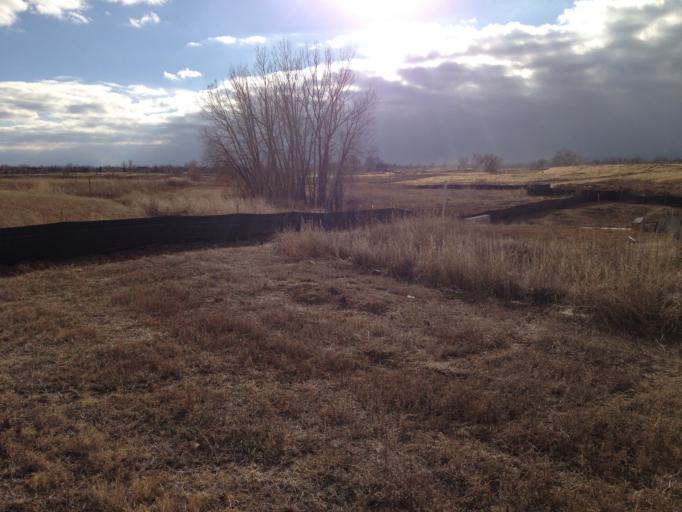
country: US
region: Colorado
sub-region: Boulder County
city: Lafayette
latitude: 40.0288
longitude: -105.0899
